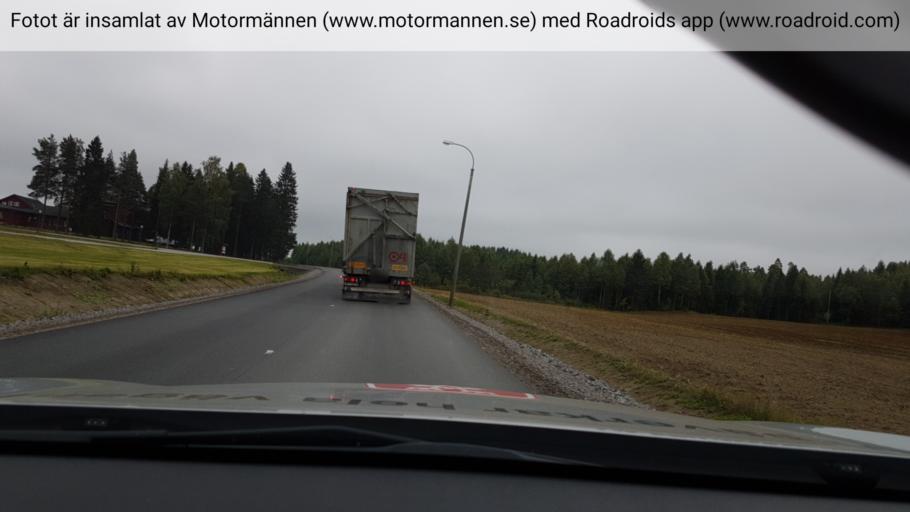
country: SE
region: Vaesterbotten
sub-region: Skelleftea Kommun
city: Burtraesk
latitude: 64.3646
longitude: 20.5009
